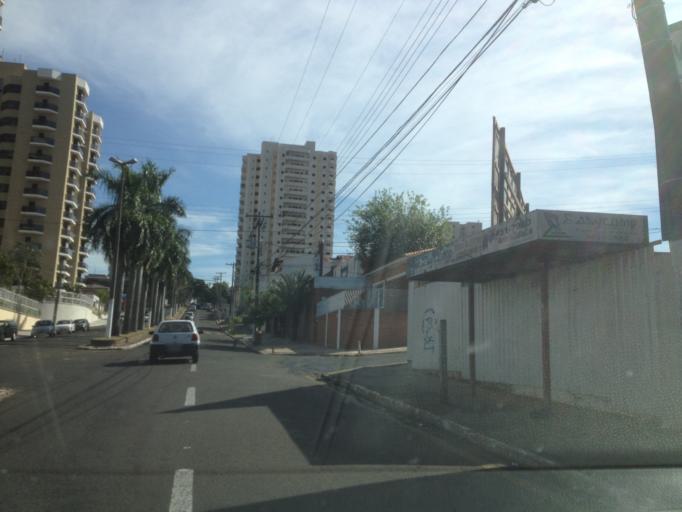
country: BR
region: Sao Paulo
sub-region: Marilia
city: Marilia
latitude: -22.2266
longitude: -49.9463
